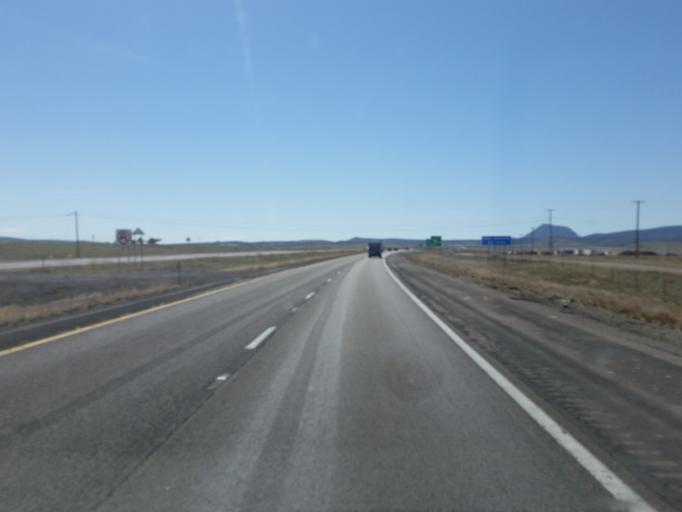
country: US
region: Arizona
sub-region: Yavapai County
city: Paulden
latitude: 35.3134
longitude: -112.8623
